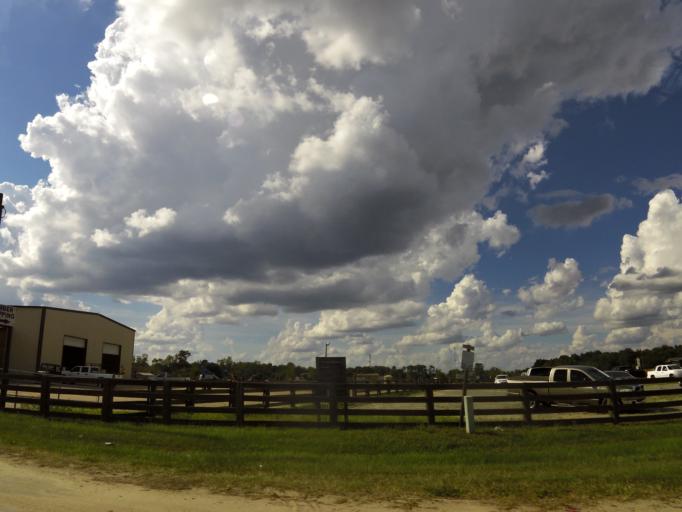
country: US
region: Georgia
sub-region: Lowndes County
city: Valdosta
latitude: 30.8170
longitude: -83.2804
